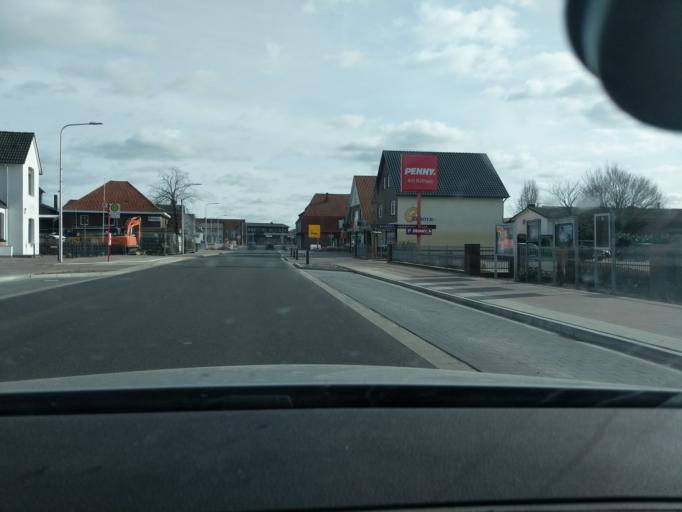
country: DE
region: Lower Saxony
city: Drochtersen
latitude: 53.7109
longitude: 9.3829
